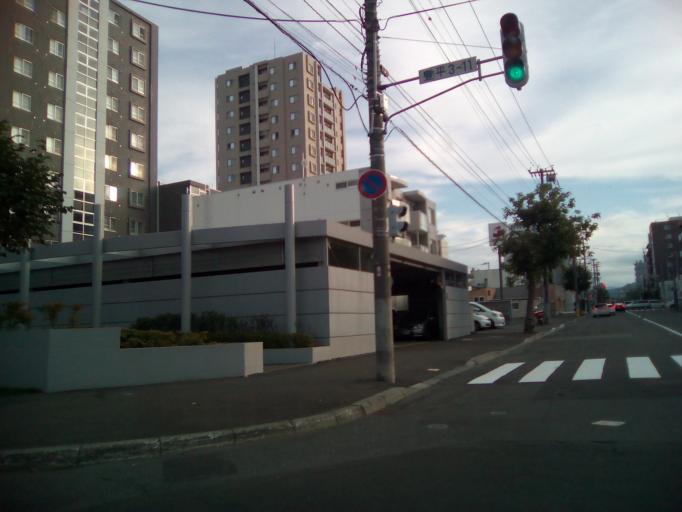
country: JP
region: Hokkaido
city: Sapporo
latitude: 43.0478
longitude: 141.3794
